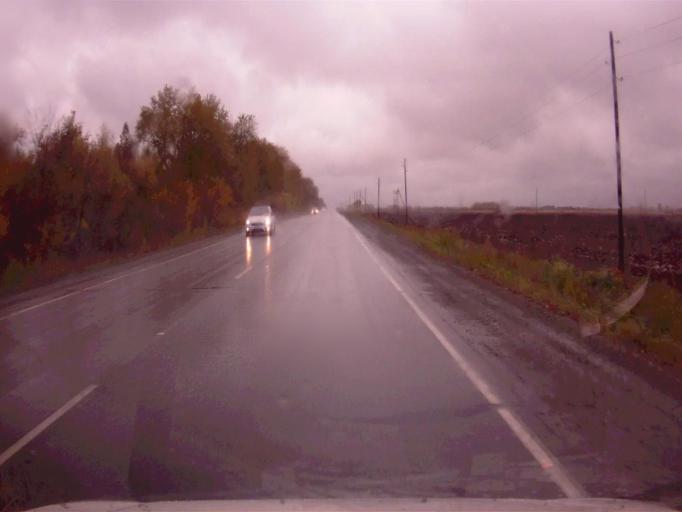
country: RU
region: Chelyabinsk
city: Argayash
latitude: 55.4293
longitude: 60.9937
